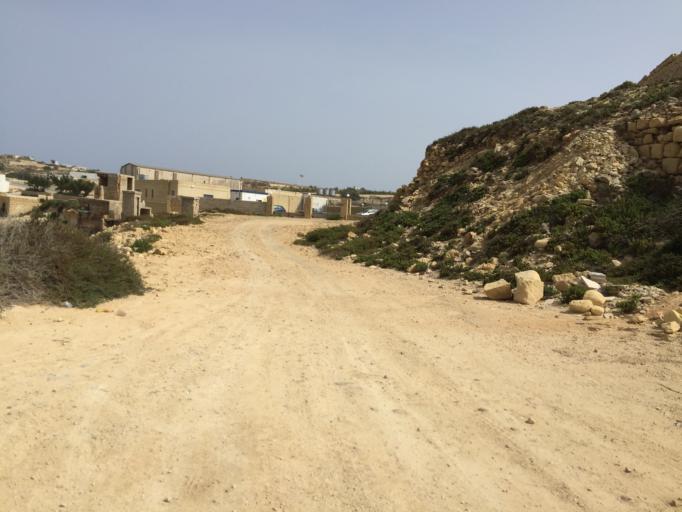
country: MT
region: Il-Kalkara
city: Kalkara
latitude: 35.8965
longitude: 14.5305
